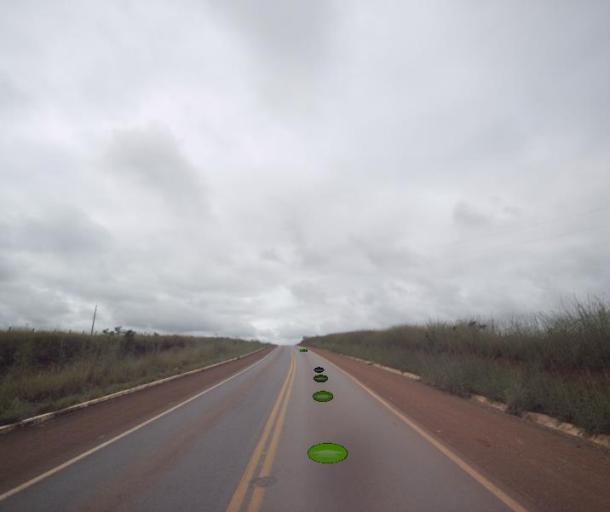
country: BR
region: Goias
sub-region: Uruacu
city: Uruacu
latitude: -14.6882
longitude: -49.1252
